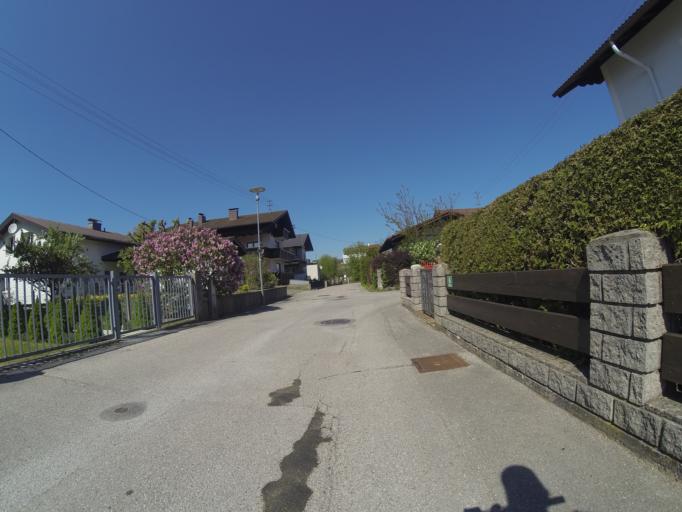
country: AT
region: Upper Austria
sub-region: Politischer Bezirk Gmunden
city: Altmunster
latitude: 47.9322
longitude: 13.7651
